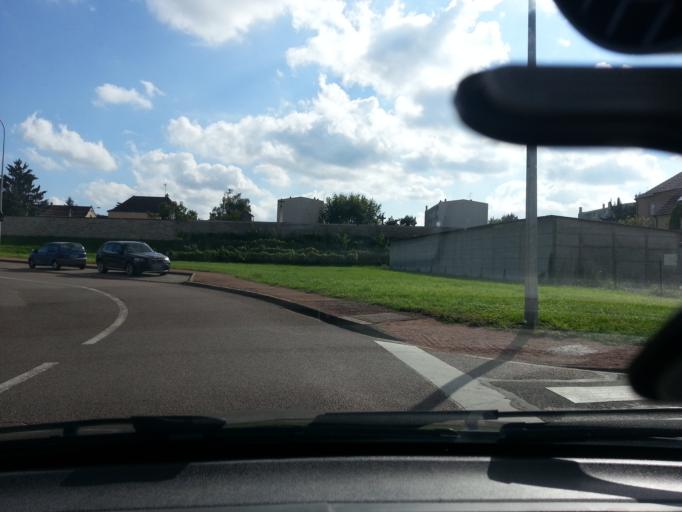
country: FR
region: Bourgogne
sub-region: Departement de Saone-et-Loire
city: Chalon-sur-Saone
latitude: 46.8004
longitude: 4.8587
